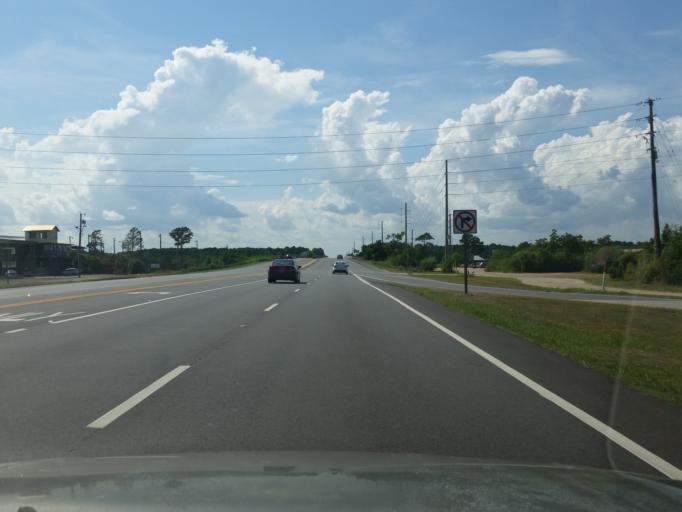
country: US
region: Alabama
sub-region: Baldwin County
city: Spanish Fort
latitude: 30.6674
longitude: -87.9205
